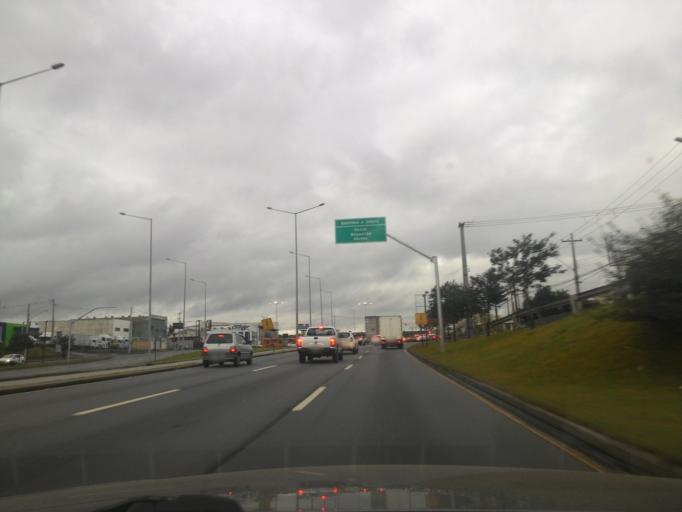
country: BR
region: Parana
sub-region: Curitiba
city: Curitiba
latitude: -25.4990
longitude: -49.2779
